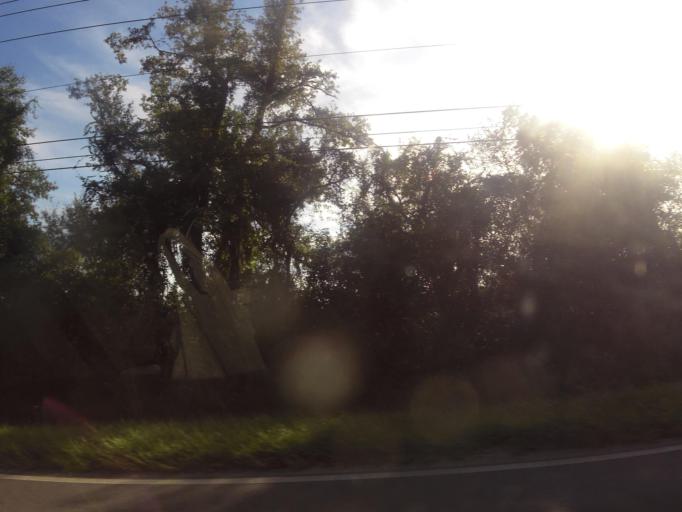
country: US
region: Florida
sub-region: Clay County
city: Green Cove Springs
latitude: 29.9092
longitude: -81.5143
